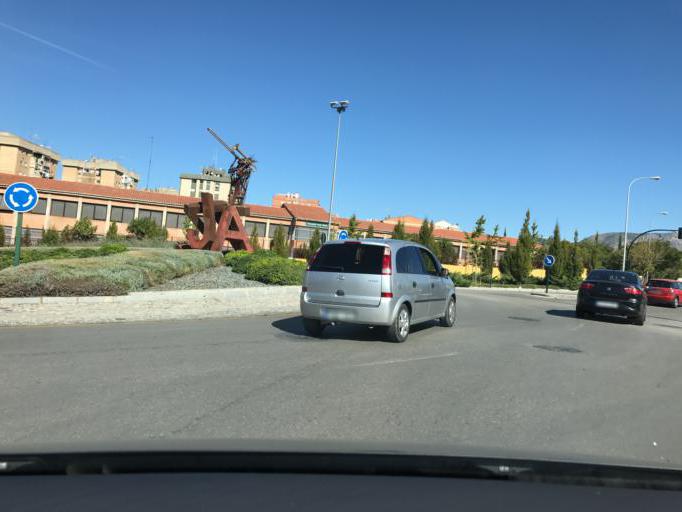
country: ES
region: Andalusia
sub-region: Provincia de Granada
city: Granada
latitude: 37.2000
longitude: -3.5996
